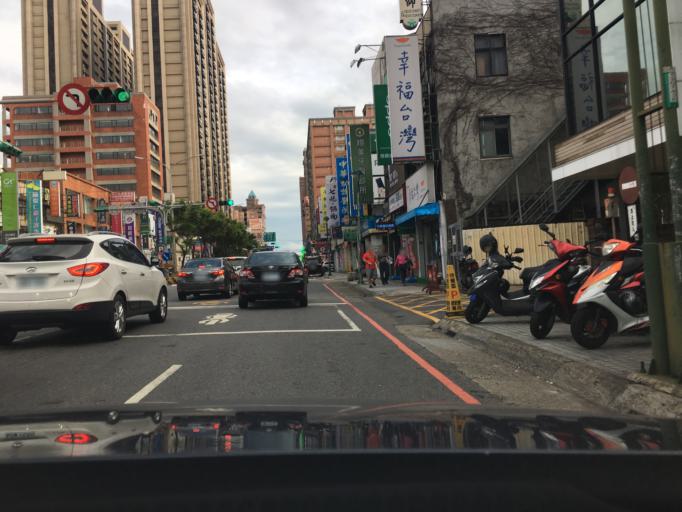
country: TW
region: Taiwan
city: Taoyuan City
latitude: 25.0470
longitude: 121.2923
